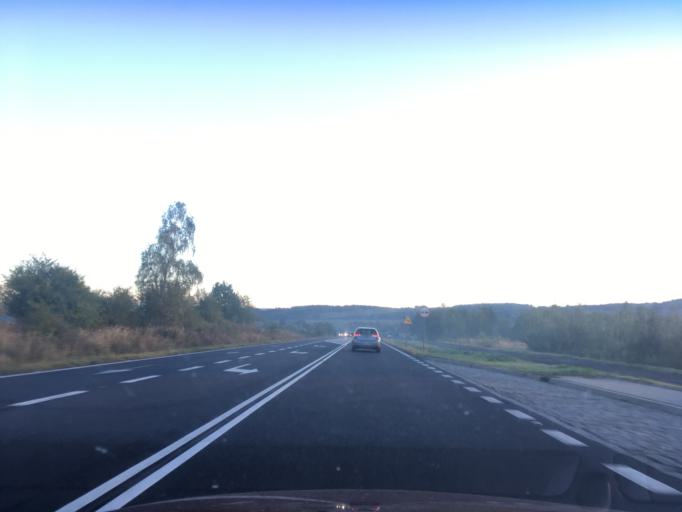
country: DE
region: Saxony
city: Ostritz
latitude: 50.9787
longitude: 14.9453
